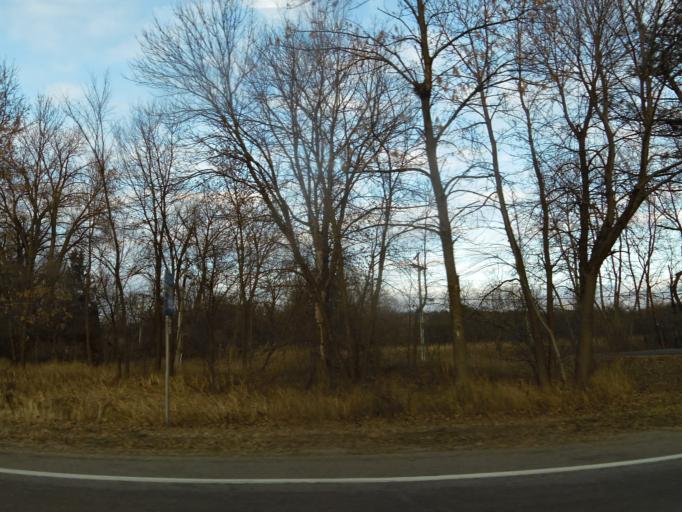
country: US
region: Minnesota
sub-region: Washington County
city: Dellwood
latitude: 45.0818
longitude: -92.9652
